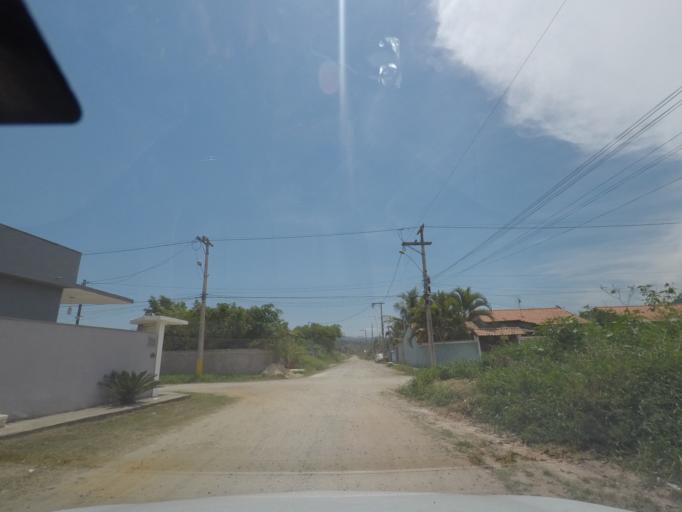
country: BR
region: Rio de Janeiro
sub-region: Marica
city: Marica
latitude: -22.9544
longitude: -42.9521
